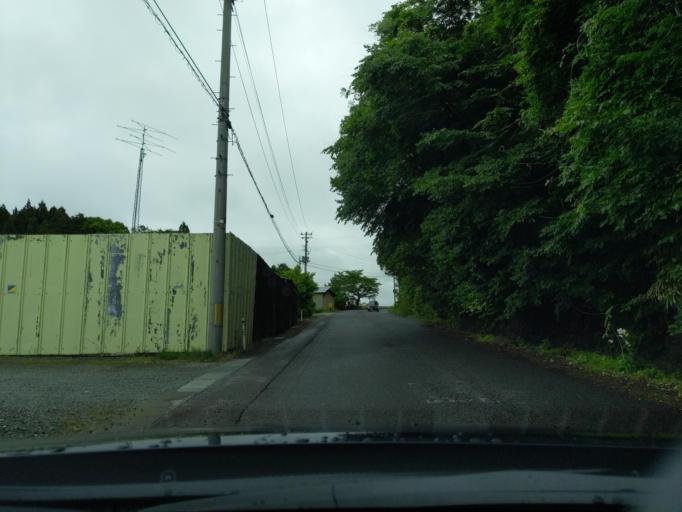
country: JP
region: Fukushima
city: Koriyama
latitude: 37.3747
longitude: 140.2910
